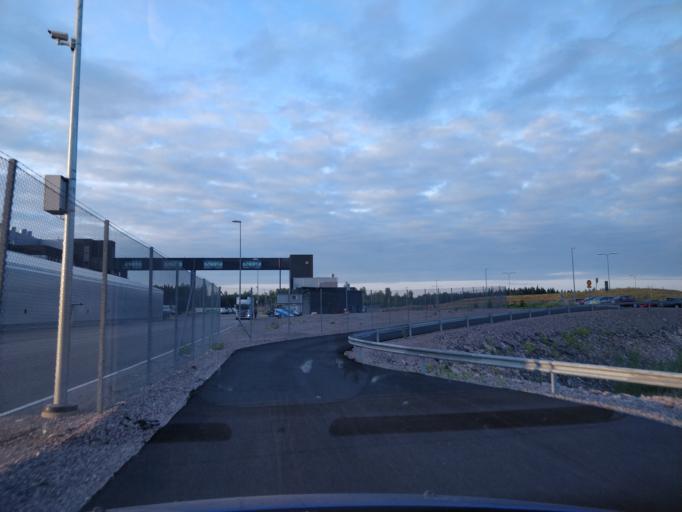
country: FI
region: Uusimaa
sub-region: Helsinki
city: Kerava
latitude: 60.3781
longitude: 25.1526
